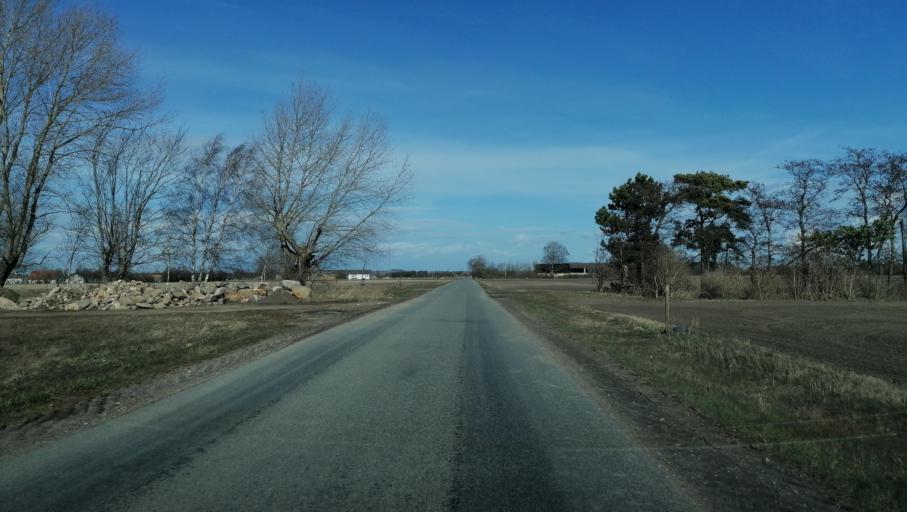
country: DK
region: Zealand
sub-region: Odsherred Kommune
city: Horve
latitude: 55.7562
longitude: 11.4921
